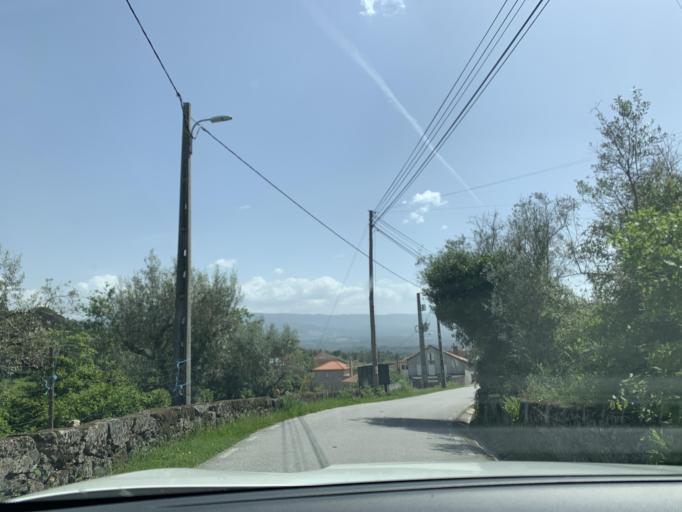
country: PT
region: Guarda
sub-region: Fornos de Algodres
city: Fornos de Algodres
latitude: 40.5919
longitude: -7.6291
